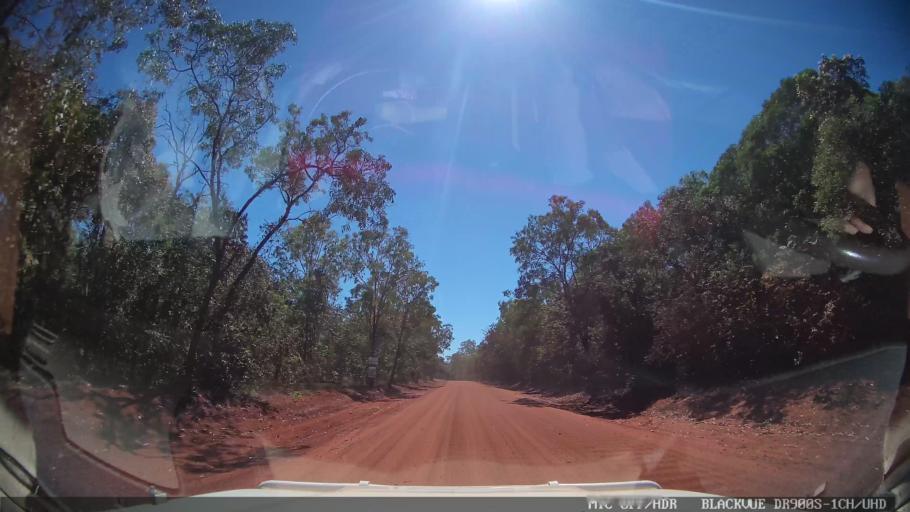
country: AU
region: Queensland
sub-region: Torres
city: Thursday Island
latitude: -10.8904
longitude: 142.4000
